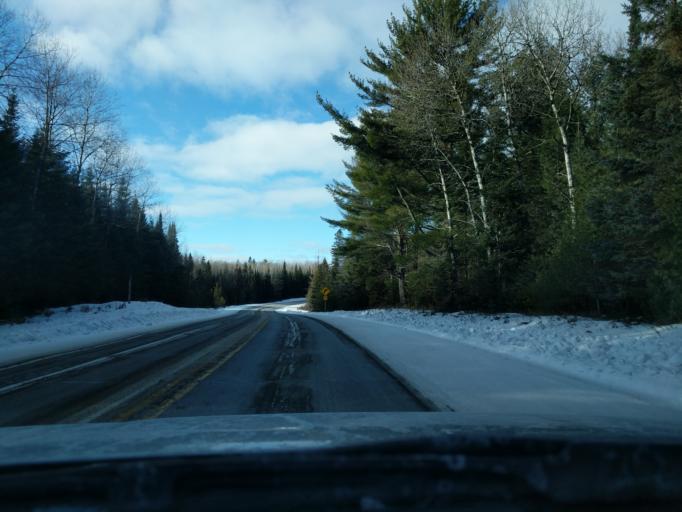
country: US
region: Wisconsin
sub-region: Vilas County
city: Eagle River
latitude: 45.7620
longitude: -89.0633
